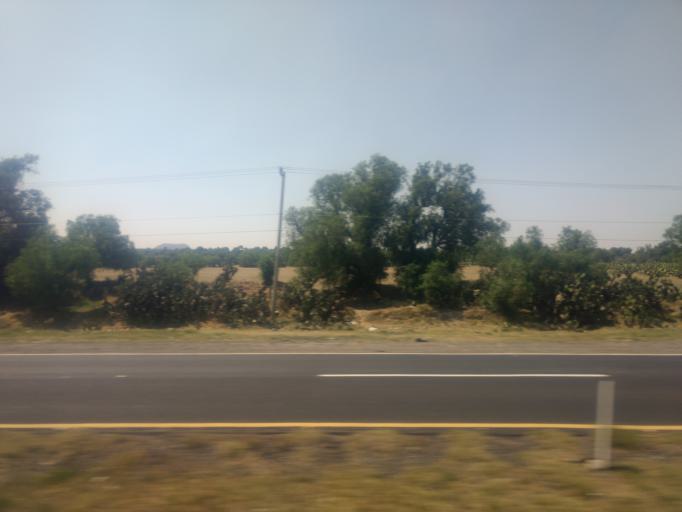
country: MX
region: Morelos
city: Nopaltepec
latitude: 19.7781
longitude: -98.7391
